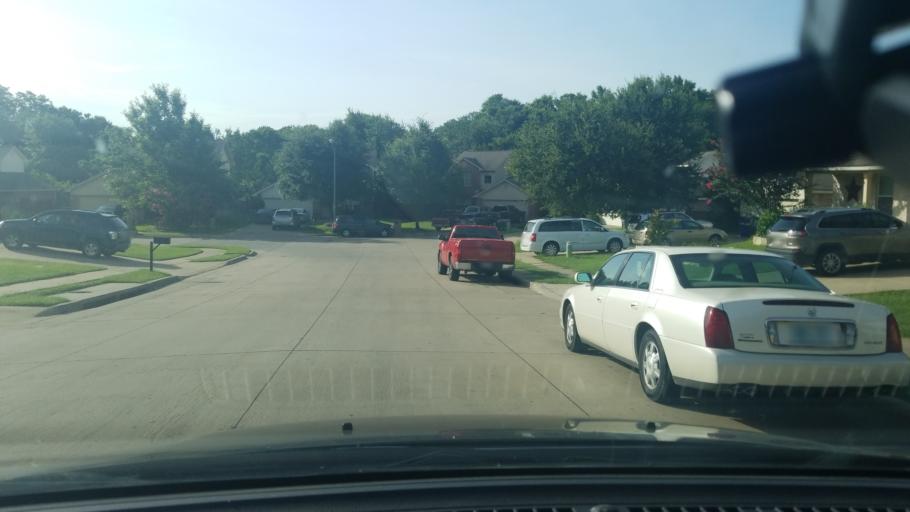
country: US
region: Texas
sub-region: Dallas County
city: Highland Park
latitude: 32.7980
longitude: -96.7142
